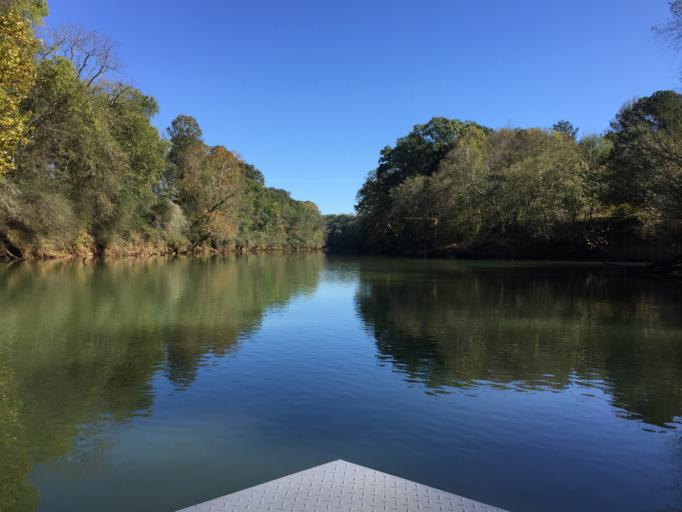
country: US
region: Georgia
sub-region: Gwinnett County
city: Duluth
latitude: 34.0340
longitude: -84.1220
